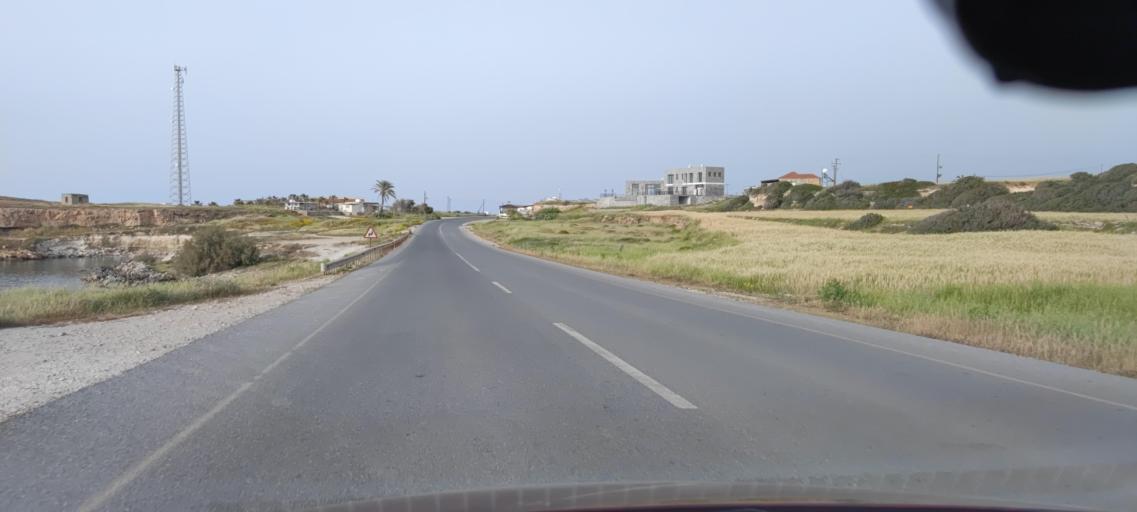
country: CY
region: Ammochostos
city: Rizokarpaso
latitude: 35.5669
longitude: 34.2494
